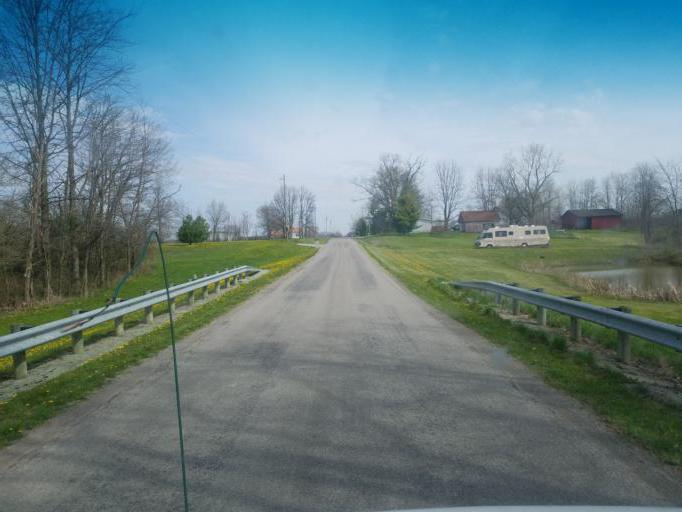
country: US
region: Ohio
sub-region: Union County
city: Richwood
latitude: 40.4710
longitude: -83.4324
